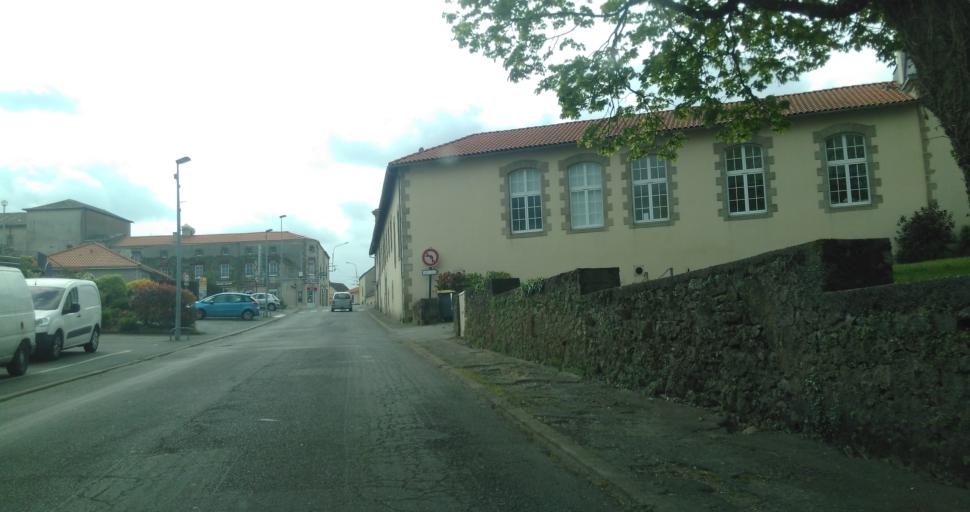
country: FR
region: Poitou-Charentes
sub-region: Departement des Deux-Sevres
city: Saint-Pierre-des-Echaubrognes
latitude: 46.9238
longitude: -0.7488
